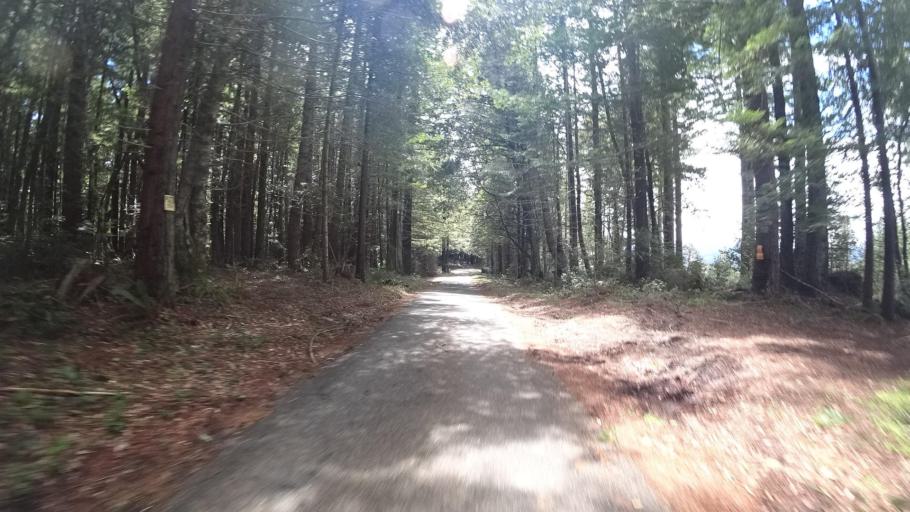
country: US
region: California
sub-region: Humboldt County
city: Blue Lake
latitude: 40.7845
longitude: -123.9635
